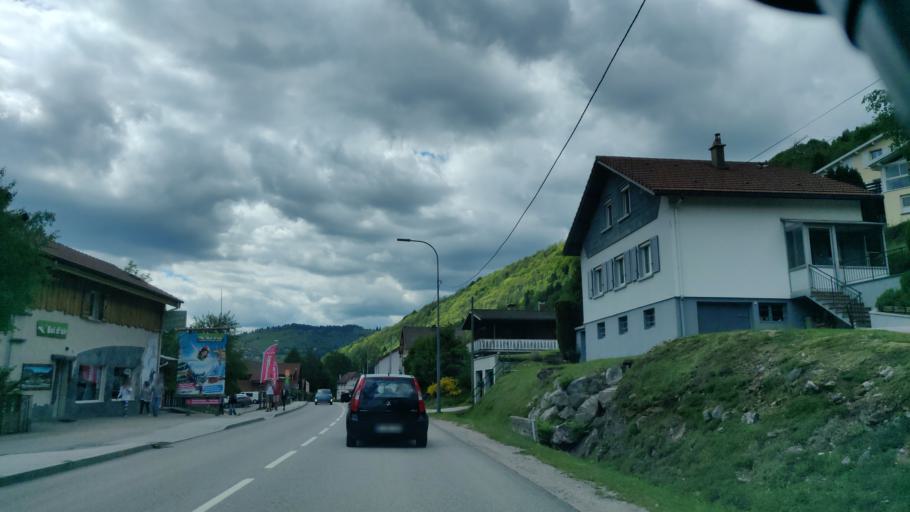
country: FR
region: Lorraine
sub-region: Departement des Vosges
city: La Bresse
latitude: 48.0027
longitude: 6.9084
